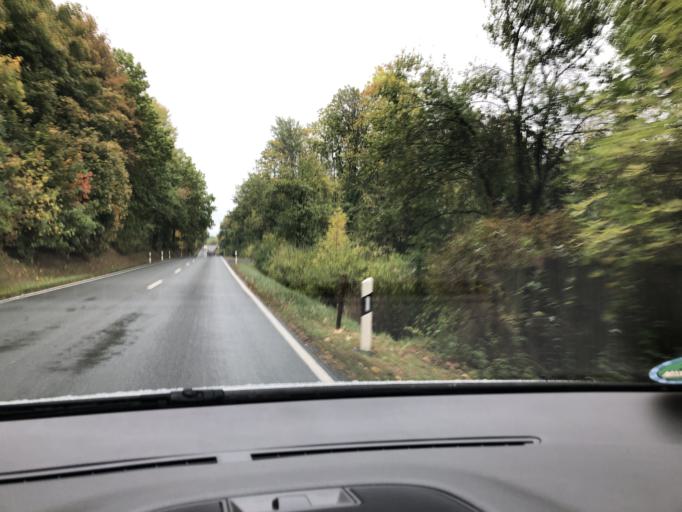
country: DE
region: Thuringia
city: Neuhaus
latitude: 50.6800
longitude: 10.9458
